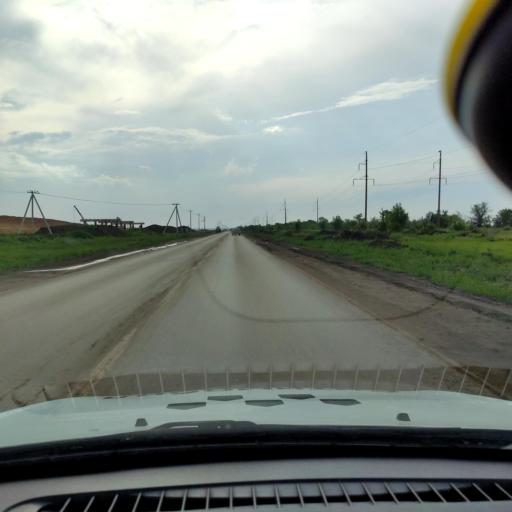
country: RU
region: Samara
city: Podstepki
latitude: 53.5614
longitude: 49.1952
